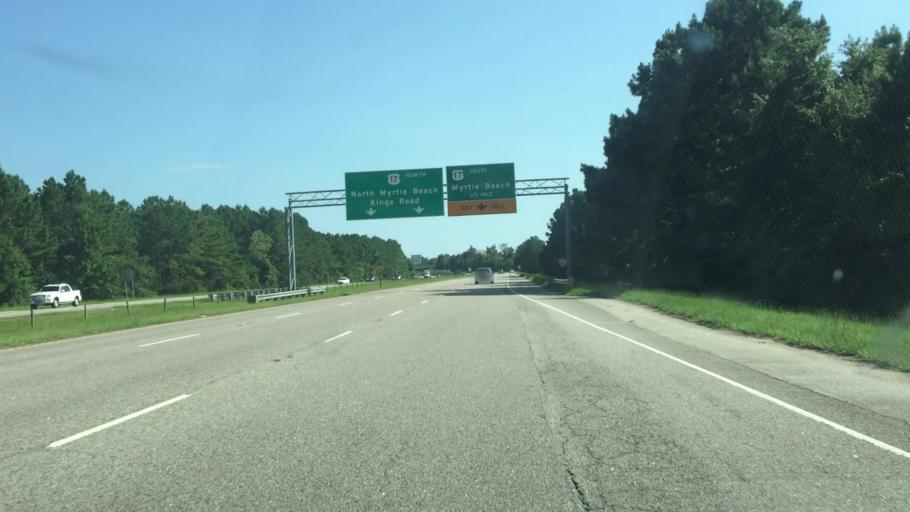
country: US
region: South Carolina
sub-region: Horry County
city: North Myrtle Beach
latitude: 33.8032
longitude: -78.7792
